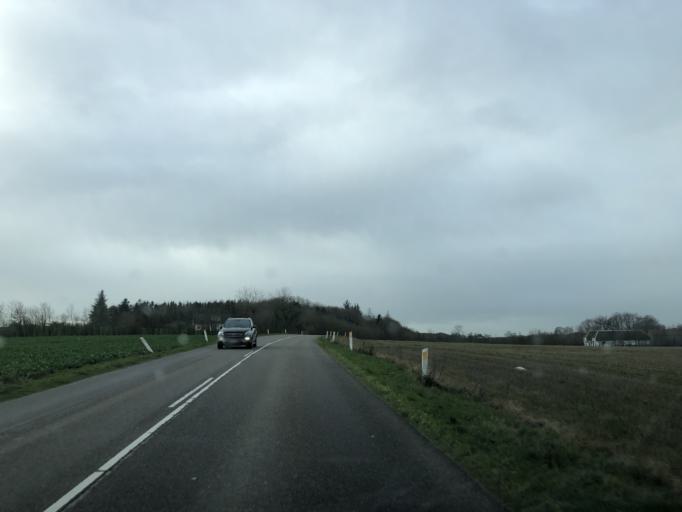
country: DK
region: North Denmark
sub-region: Rebild Kommune
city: Stovring
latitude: 56.8819
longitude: 9.7747
